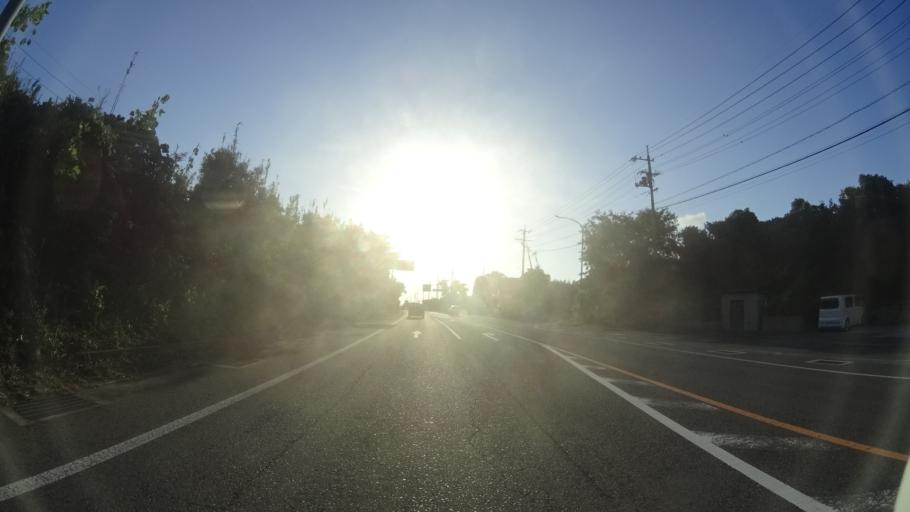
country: JP
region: Tottori
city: Yonago
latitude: 35.5140
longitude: 133.5167
